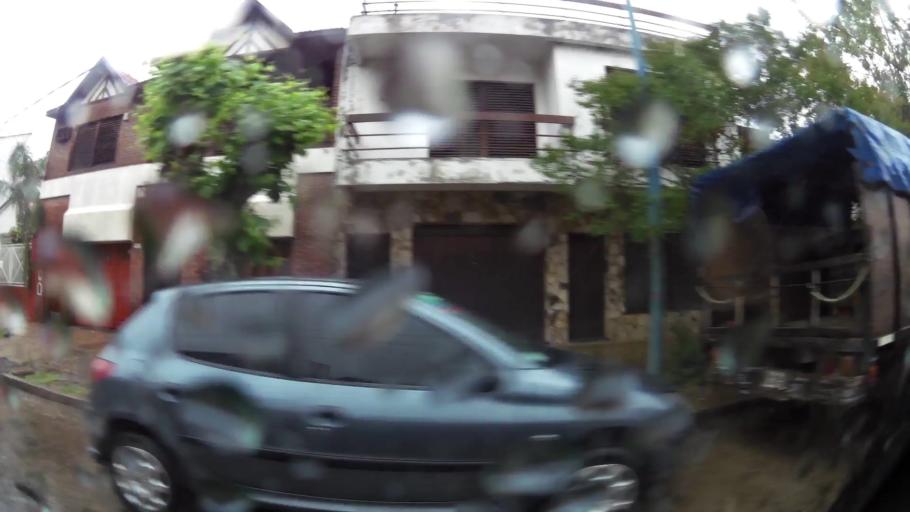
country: AR
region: Buenos Aires
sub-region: Partido de Lanus
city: Lanus
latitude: -34.7127
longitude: -58.4013
